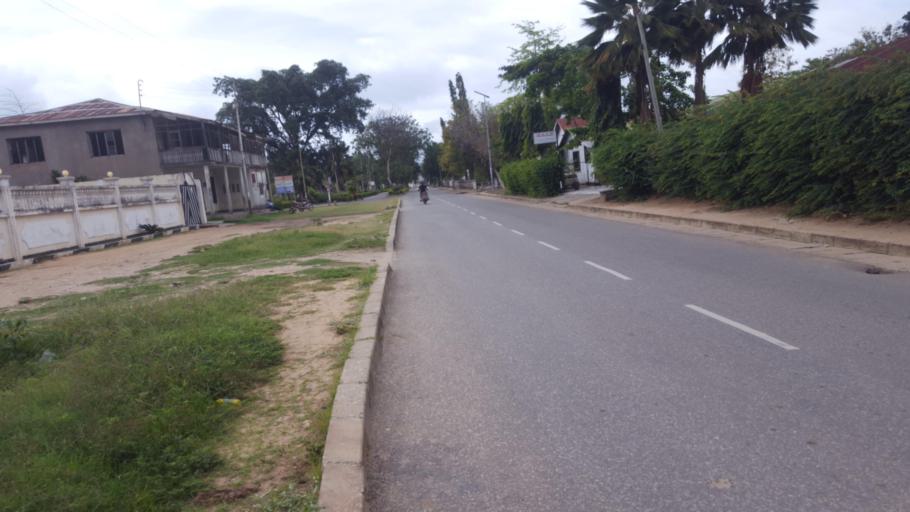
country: TZ
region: Tanga
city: Tanga
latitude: -5.0695
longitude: 39.0963
